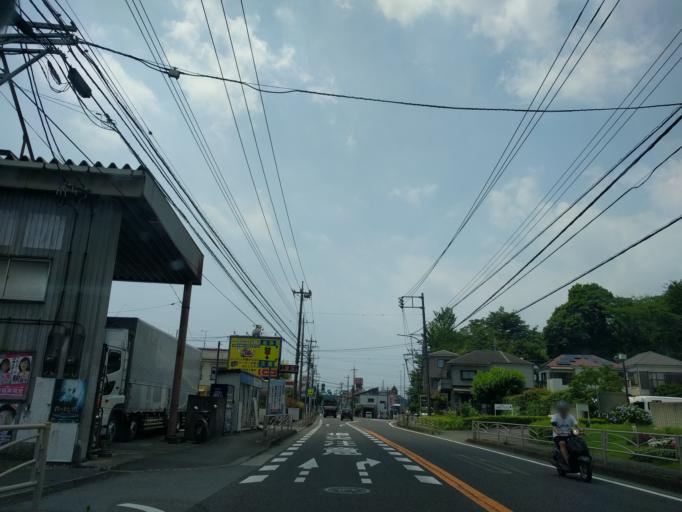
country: JP
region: Kanagawa
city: Minami-rinkan
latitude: 35.4934
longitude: 139.5098
